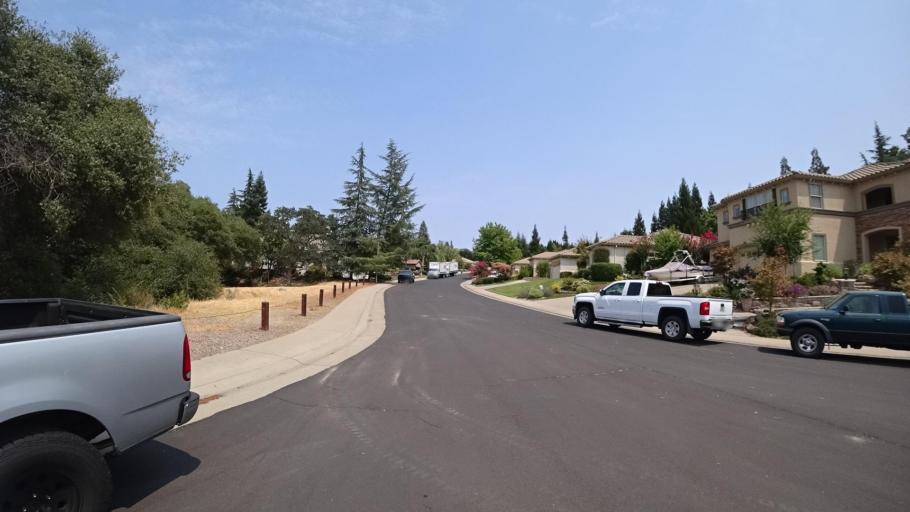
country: US
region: California
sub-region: Placer County
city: Rocklin
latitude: 38.7708
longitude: -121.2247
